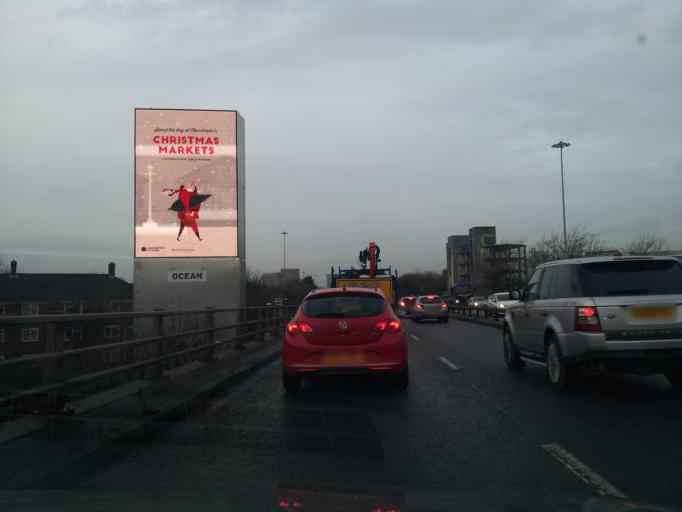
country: GB
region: England
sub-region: Manchester
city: Hulme
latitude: 53.4704
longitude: -2.2466
